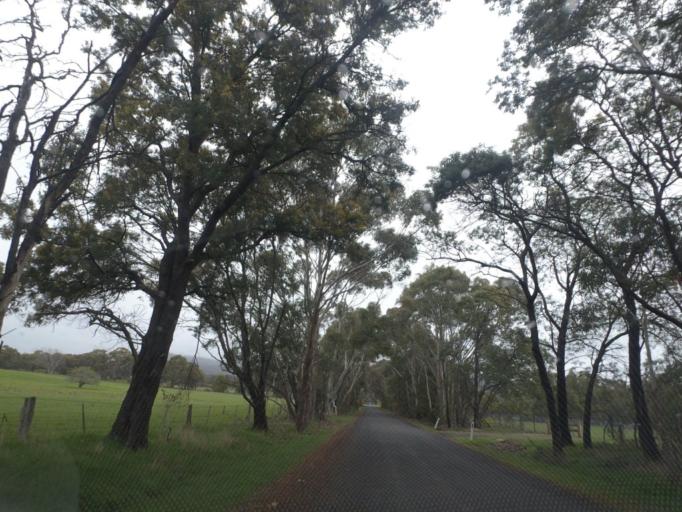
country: AU
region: Victoria
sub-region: Hume
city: Sunbury
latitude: -37.3334
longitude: 144.6050
